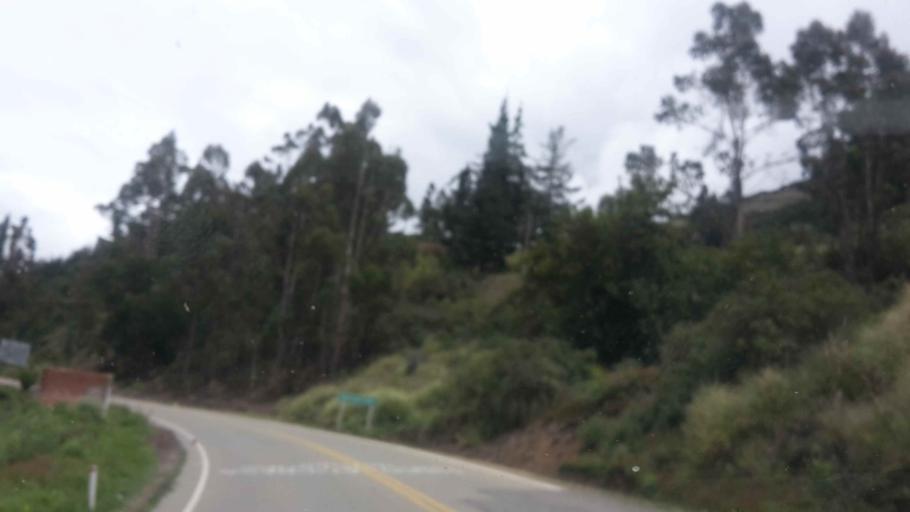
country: BO
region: Cochabamba
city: Arani
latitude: -17.4876
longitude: -65.4630
